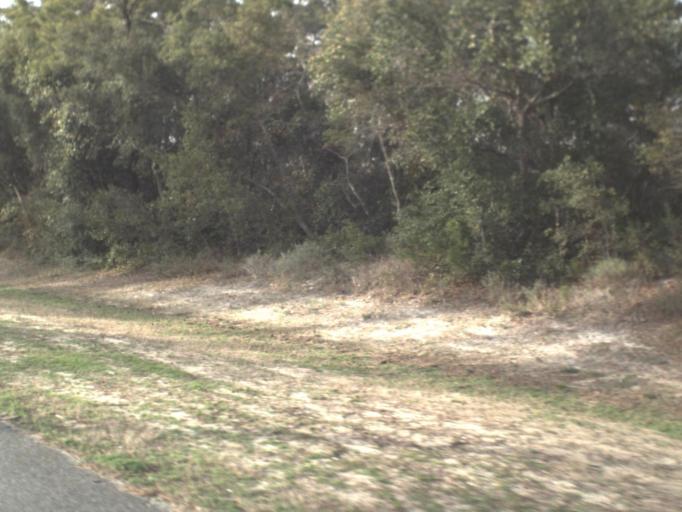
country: US
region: Florida
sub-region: Bay County
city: Mexico Beach
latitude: 29.9577
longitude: -85.4345
